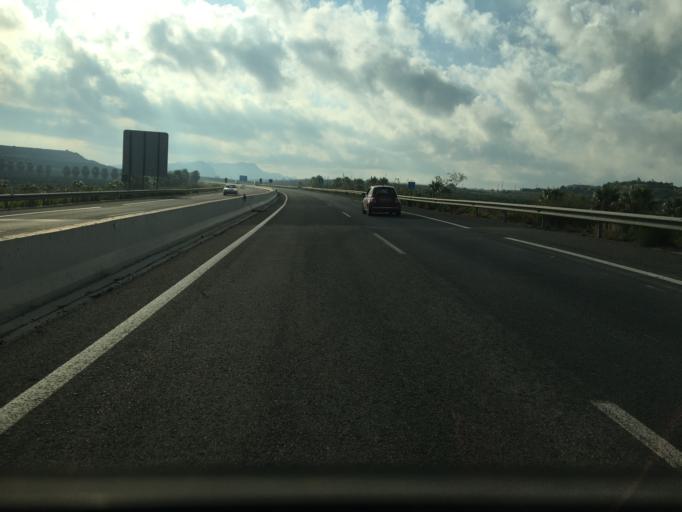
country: ES
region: Murcia
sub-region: Murcia
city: Beniel
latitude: 37.9953
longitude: -1.0007
